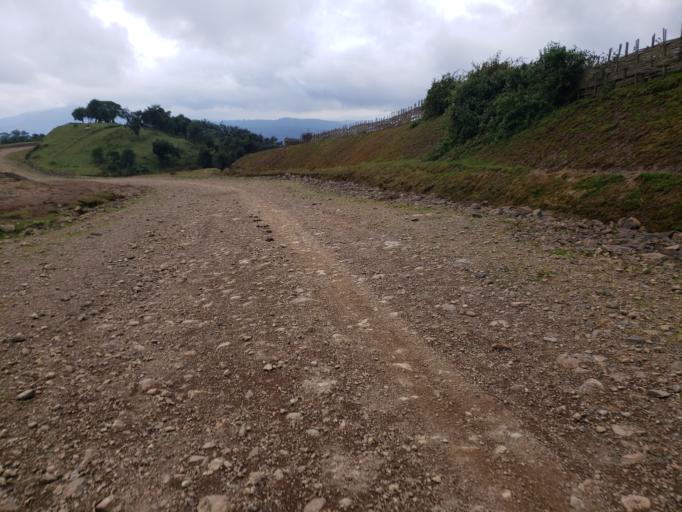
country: ET
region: Oromiya
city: Dodola
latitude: 6.6961
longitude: 39.3688
